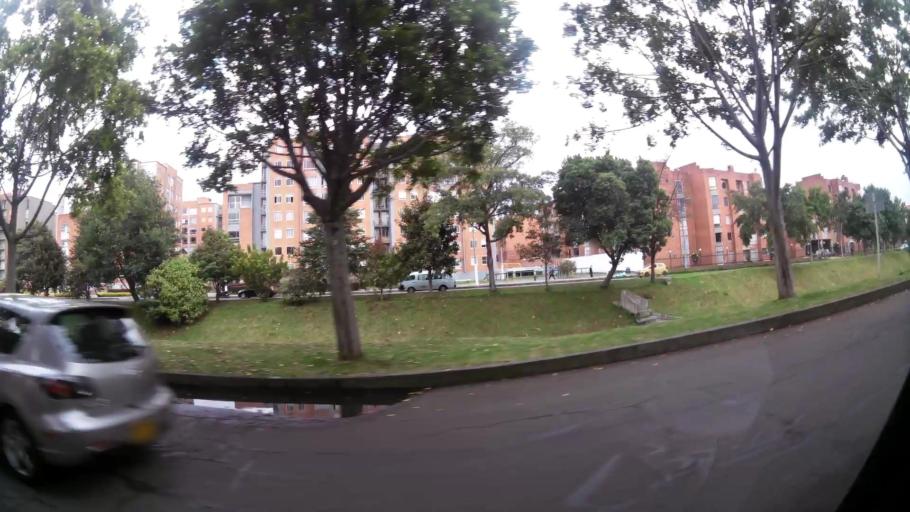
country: CO
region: Bogota D.C.
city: Barrio San Luis
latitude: 4.7368
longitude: -74.0554
